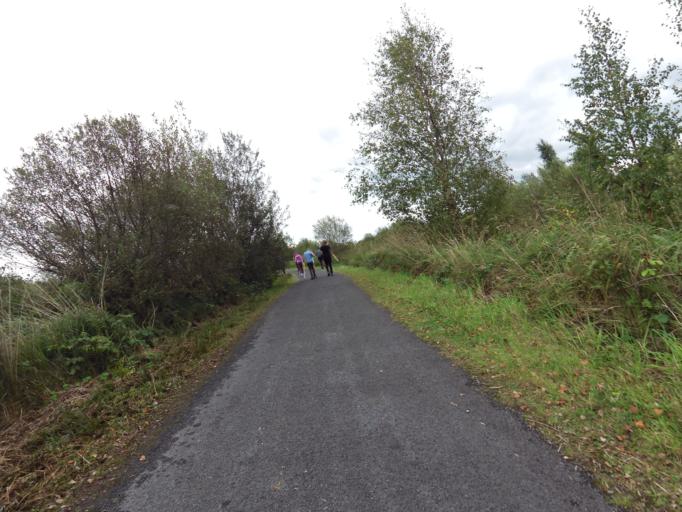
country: IE
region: Leinster
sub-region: Uibh Fhaili
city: Ferbane
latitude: 53.2223
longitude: -7.7361
